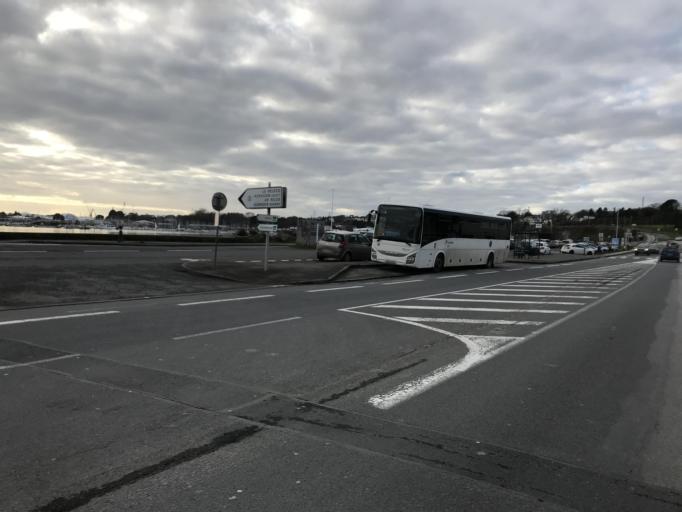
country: FR
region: Brittany
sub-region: Departement du Finistere
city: Le Relecq-Kerhuon
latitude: 48.3968
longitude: -4.4209
